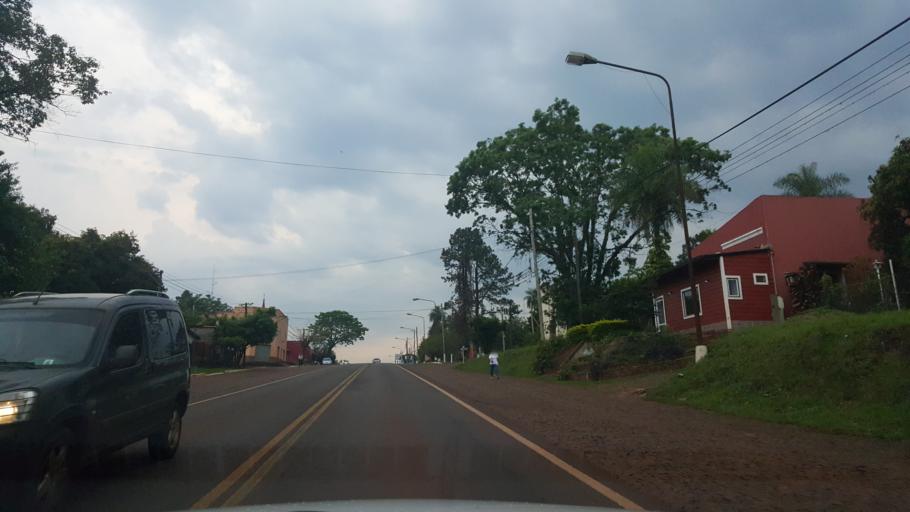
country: AR
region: Misiones
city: Gobernador Roca
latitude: -27.1925
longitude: -55.4713
